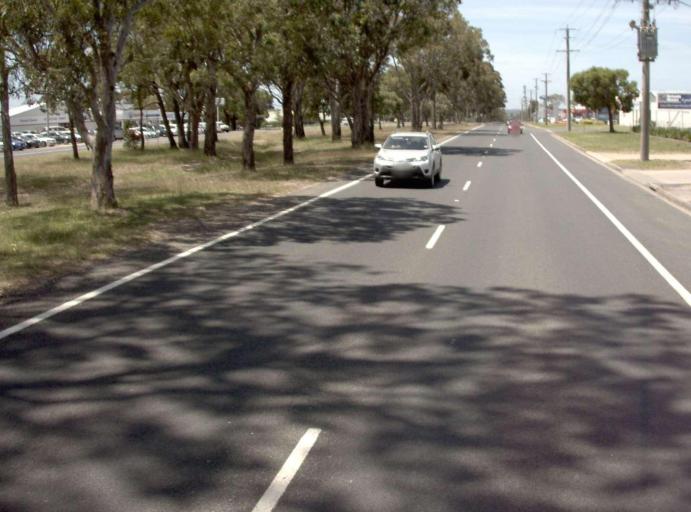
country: AU
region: Victoria
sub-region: East Gippsland
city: Bairnsdale
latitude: -37.8346
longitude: 147.6041
